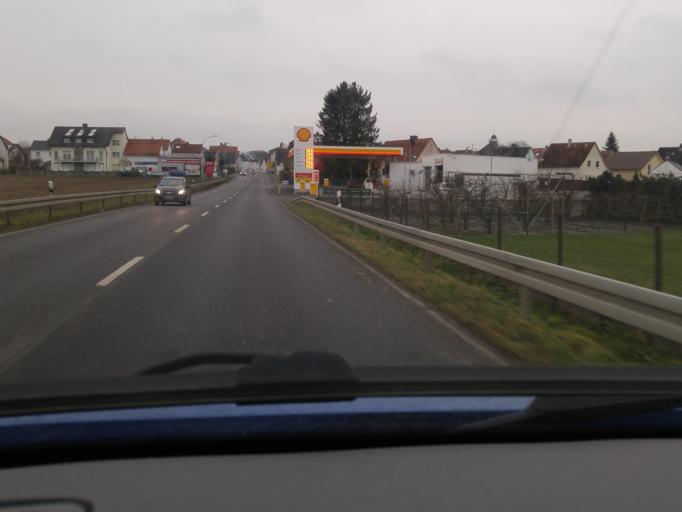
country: DE
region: Hesse
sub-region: Regierungsbezirk Darmstadt
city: Florstadt
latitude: 50.3229
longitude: 8.8506
